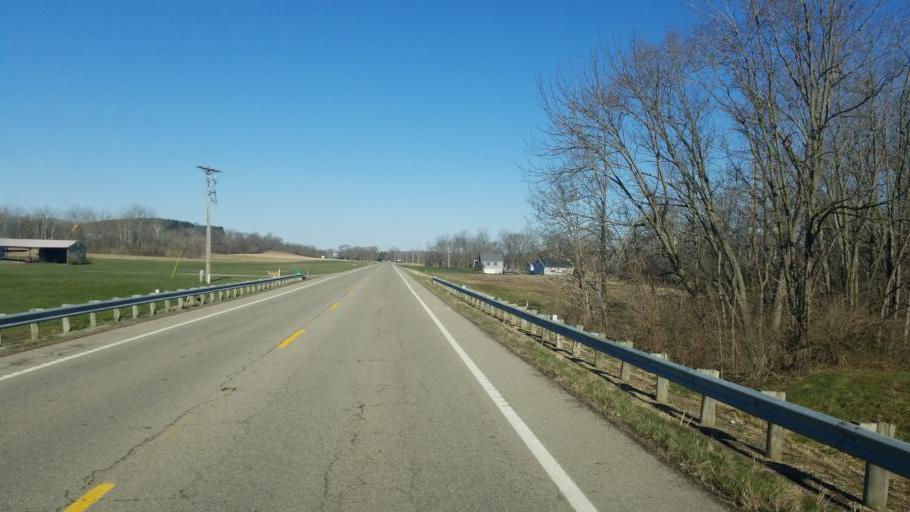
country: US
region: Ohio
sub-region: Highland County
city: Greenfield
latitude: 39.2249
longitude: -83.3138
